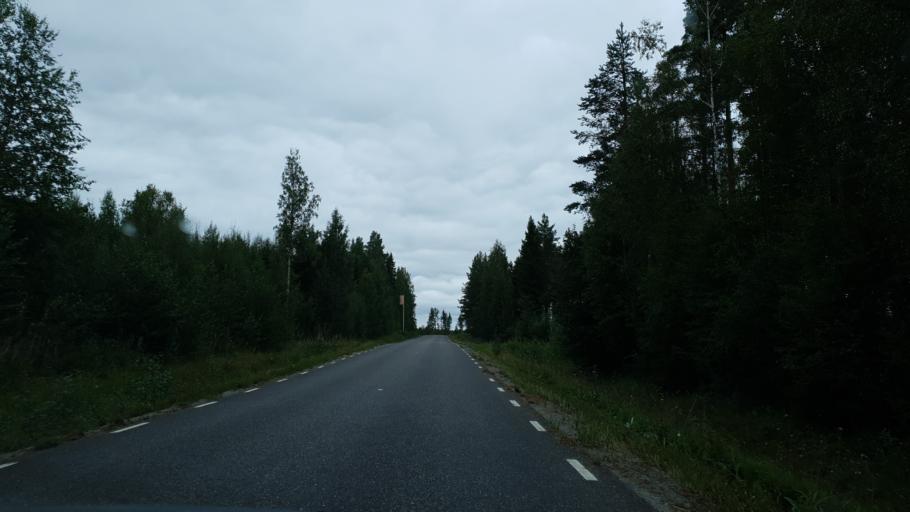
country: SE
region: Vaesterbotten
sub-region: Skelleftea Kommun
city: Viken
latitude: 64.7983
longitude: 20.7427
